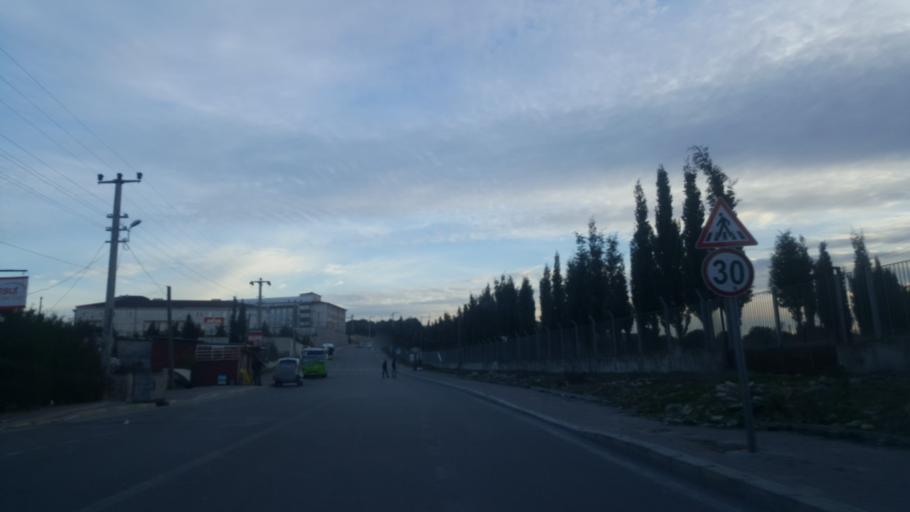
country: TR
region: Kocaeli
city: Tavsancil
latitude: 40.7942
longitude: 29.5515
